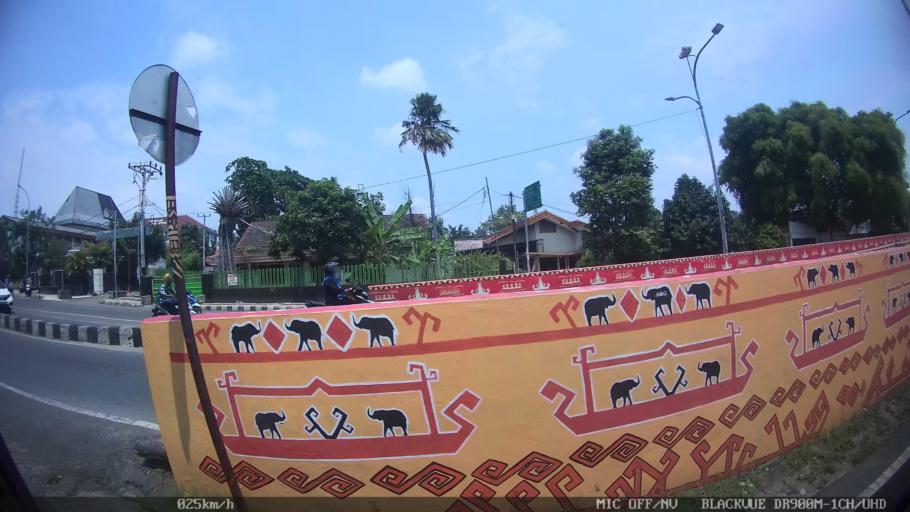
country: ID
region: Lampung
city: Bandarlampung
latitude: -5.4236
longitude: 105.2695
